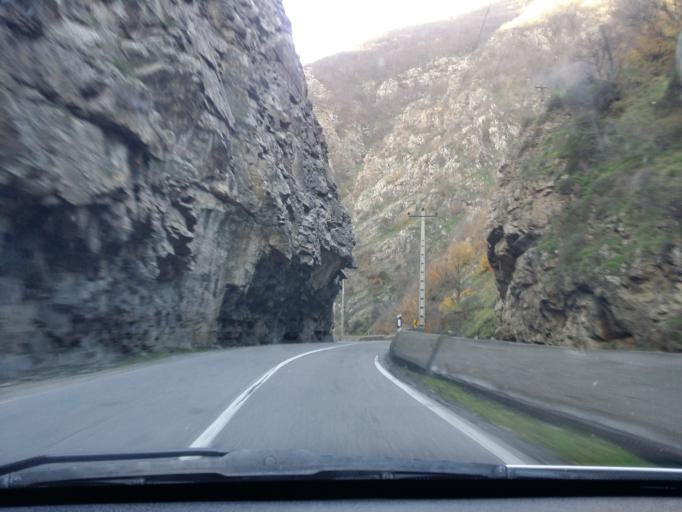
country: IR
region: Mazandaran
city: Chalus
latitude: 36.2917
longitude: 51.2395
